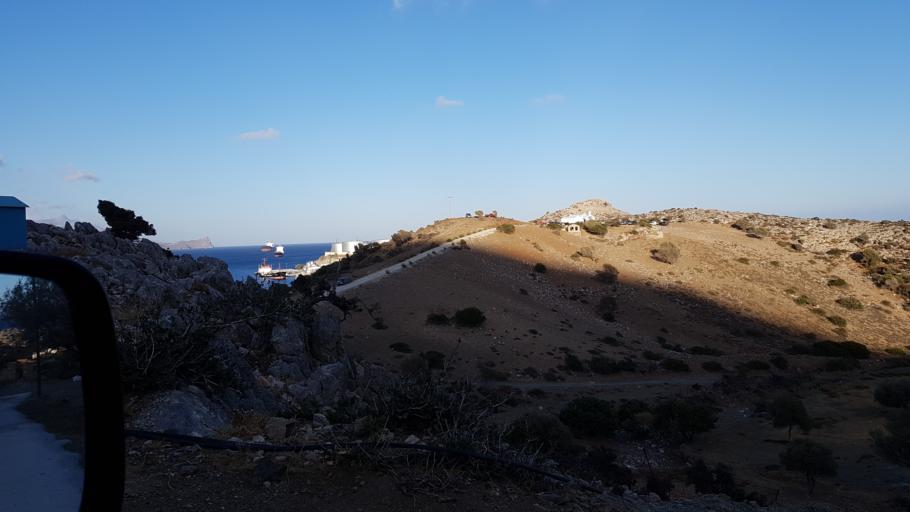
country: GR
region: Crete
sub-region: Nomos Irakleiou
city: Moires
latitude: 34.9292
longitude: 24.7973
